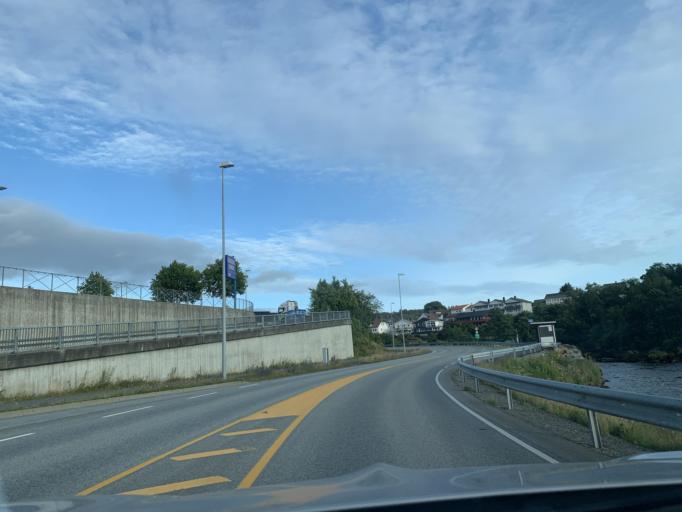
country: NO
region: Rogaland
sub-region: Eigersund
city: Egersund
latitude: 58.4614
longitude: 6.0112
